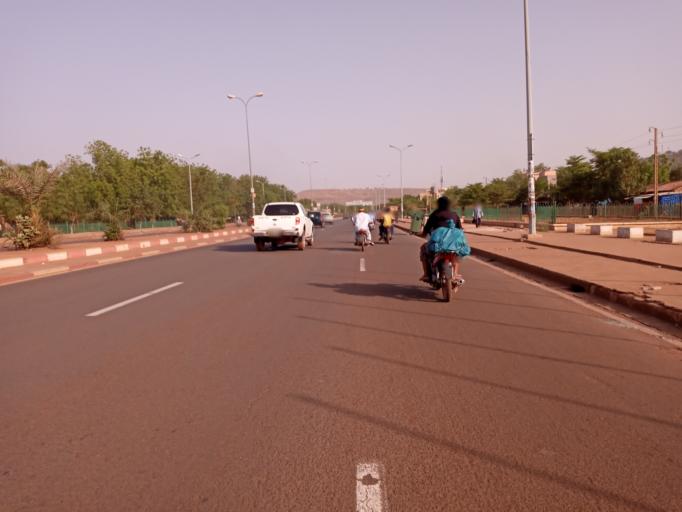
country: ML
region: Bamako
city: Bamako
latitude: 12.6427
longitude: -8.0077
